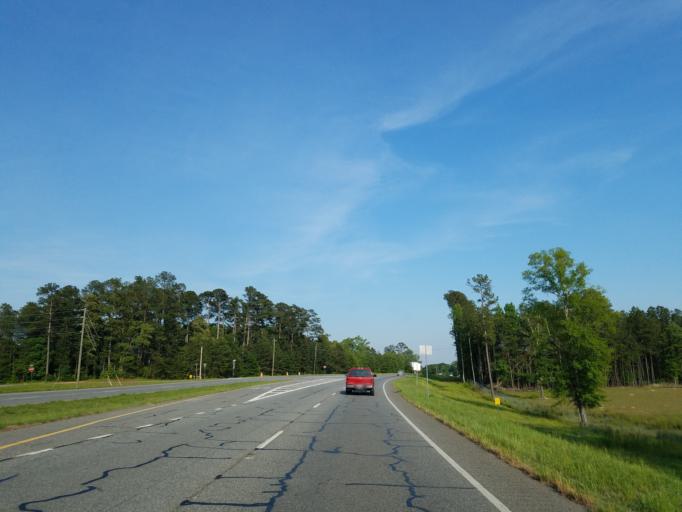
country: US
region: Georgia
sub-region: Floyd County
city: Rome
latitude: 34.3994
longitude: -85.2074
